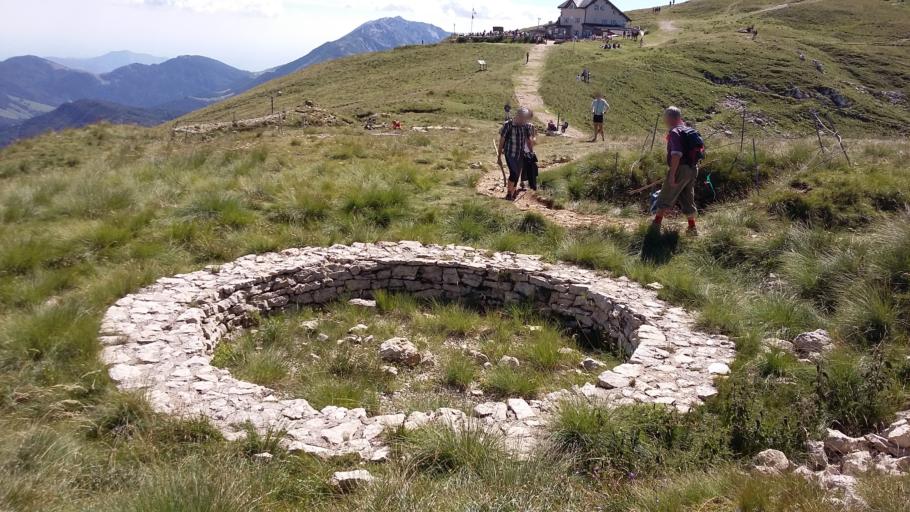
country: IT
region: Trentino-Alto Adige
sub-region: Provincia di Trento
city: Torbole sul Garda
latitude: 45.8118
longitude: 10.8917
